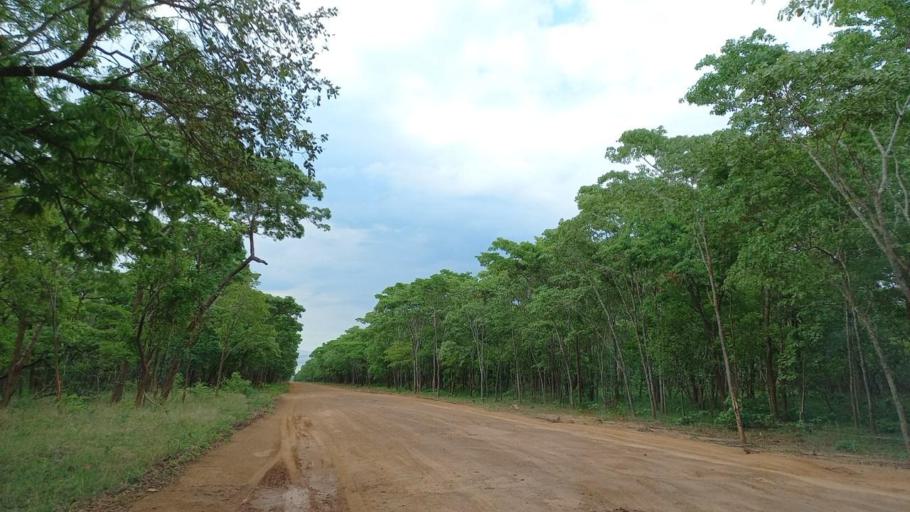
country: ZM
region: North-Western
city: Kalengwa
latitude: -13.3581
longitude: 25.0764
